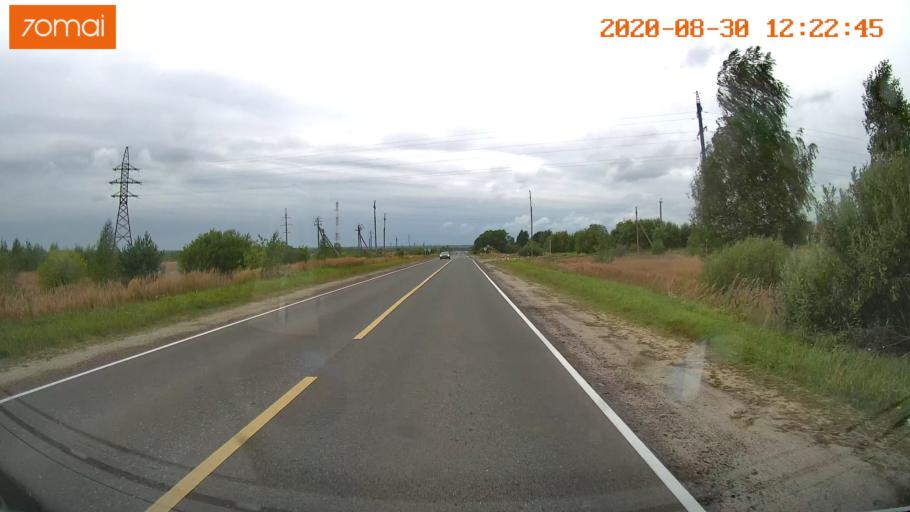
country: RU
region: Ivanovo
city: Yur'yevets
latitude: 57.3308
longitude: 42.8415
